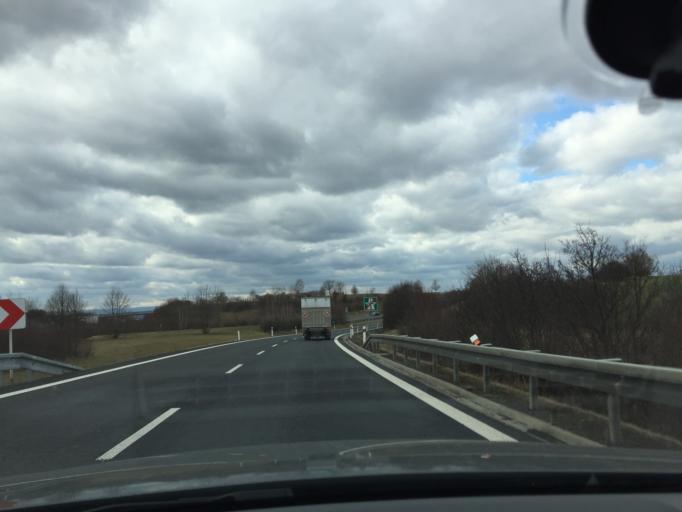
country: CZ
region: Olomoucky
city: Praslavice
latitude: 49.5781
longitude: 17.3846
